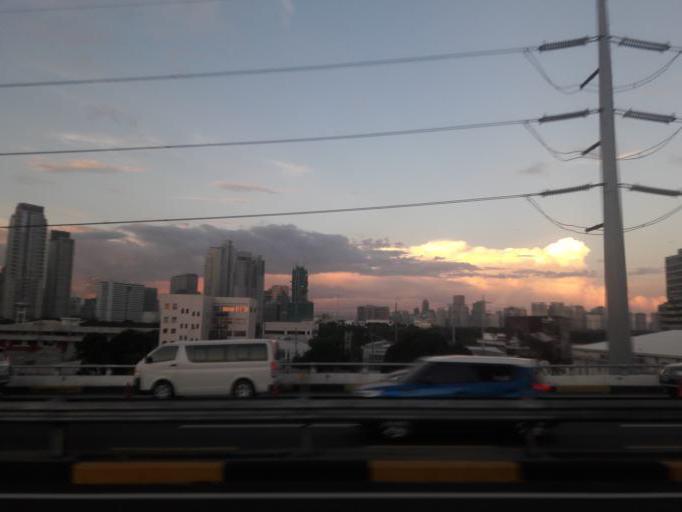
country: PH
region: Metro Manila
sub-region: Makati City
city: Makati City
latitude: 14.5435
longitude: 121.0153
